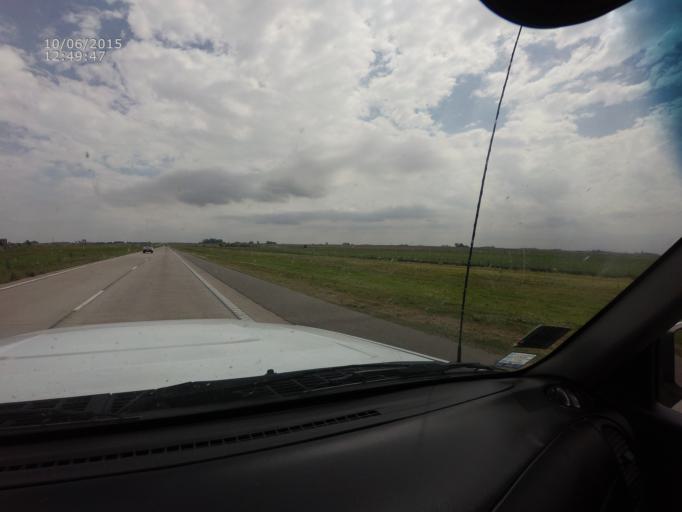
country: AR
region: Santa Fe
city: Canada de Gomez
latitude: -32.8316
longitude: -61.4776
